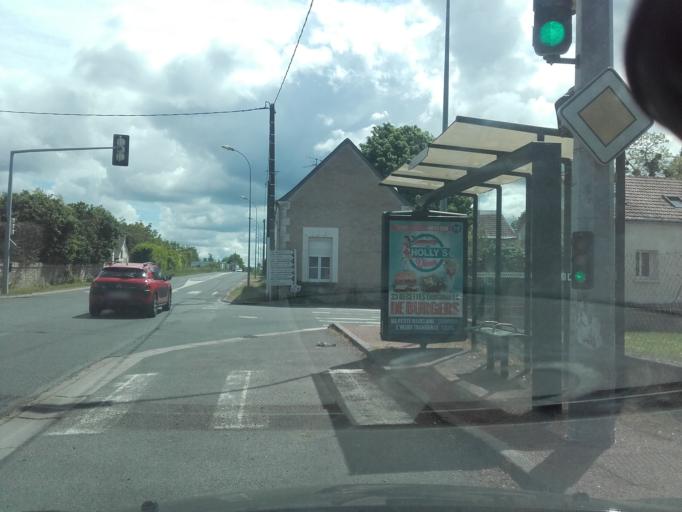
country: FR
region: Centre
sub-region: Departement d'Indre-et-Loire
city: Azay-sur-Cher
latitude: 47.3493
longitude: 0.8369
